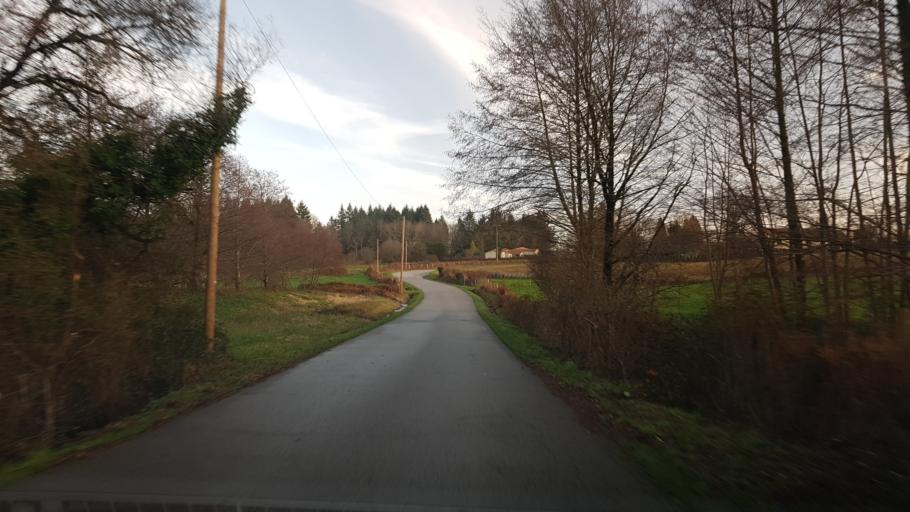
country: FR
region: Limousin
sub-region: Departement de la Haute-Vienne
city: Saint-Junien
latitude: 45.8992
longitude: 0.8605
